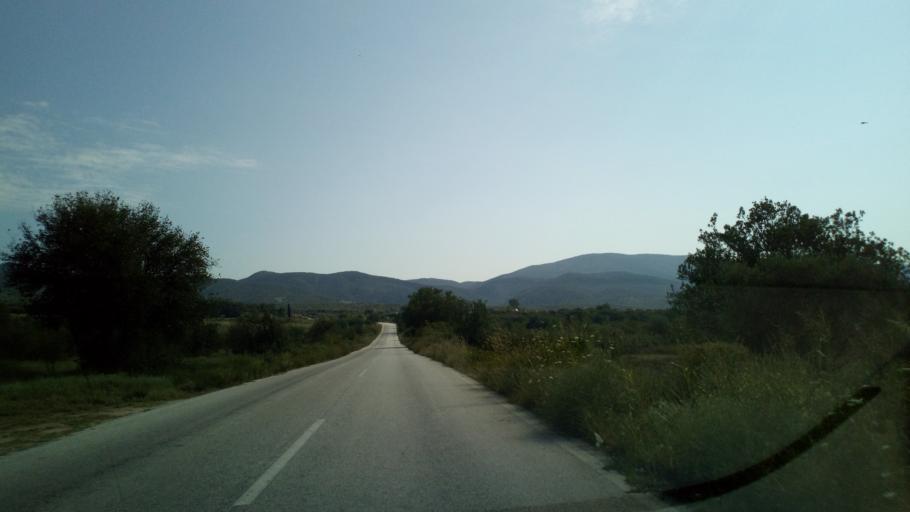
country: GR
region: Central Macedonia
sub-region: Nomos Thessalonikis
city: Askos
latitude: 40.7082
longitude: 23.3749
